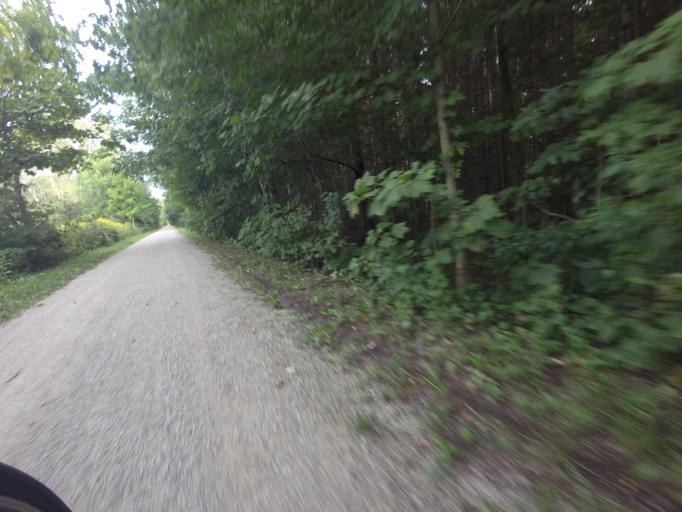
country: CA
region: Ontario
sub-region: Wellington County
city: Guelph
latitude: 43.5709
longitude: -80.3404
